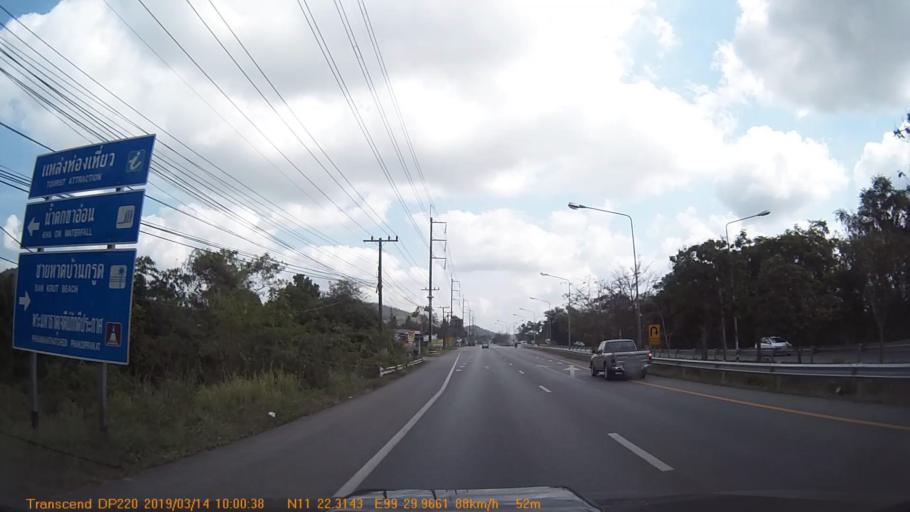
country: TH
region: Prachuap Khiri Khan
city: Bang Saphan
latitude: 11.3722
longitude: 99.4996
